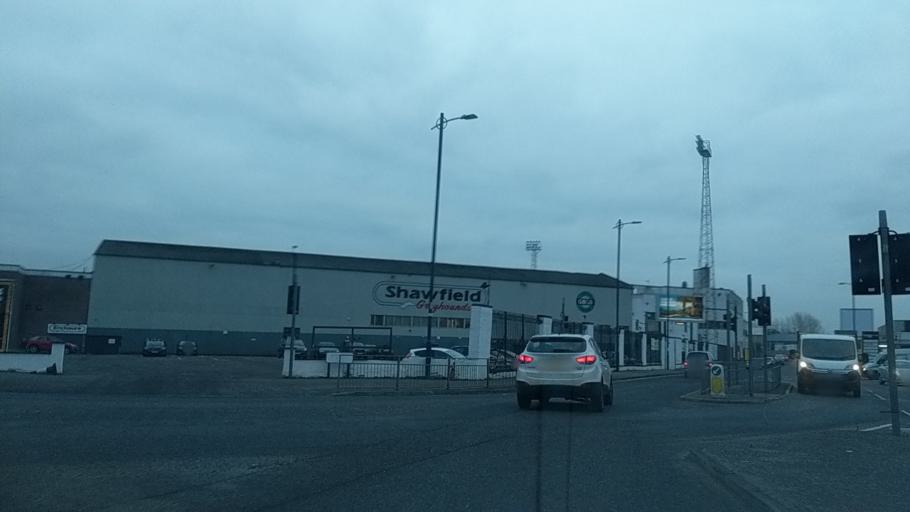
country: GB
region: Scotland
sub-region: South Lanarkshire
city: Rutherglen
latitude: 55.8382
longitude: -4.2313
